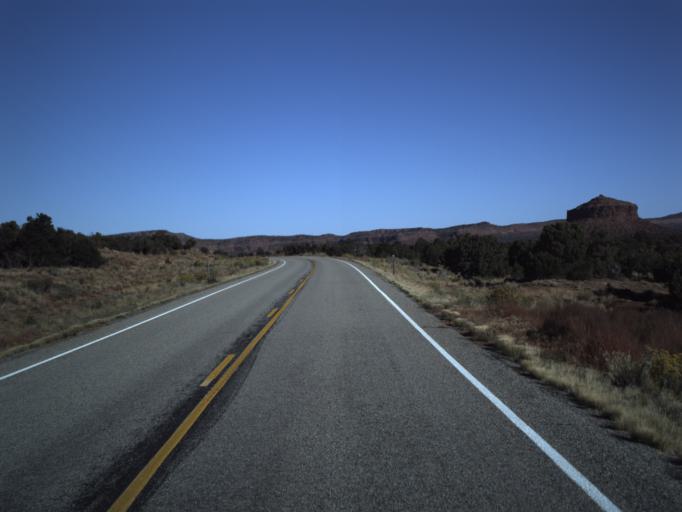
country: US
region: Utah
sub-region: San Juan County
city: Blanding
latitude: 37.6265
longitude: -110.0865
